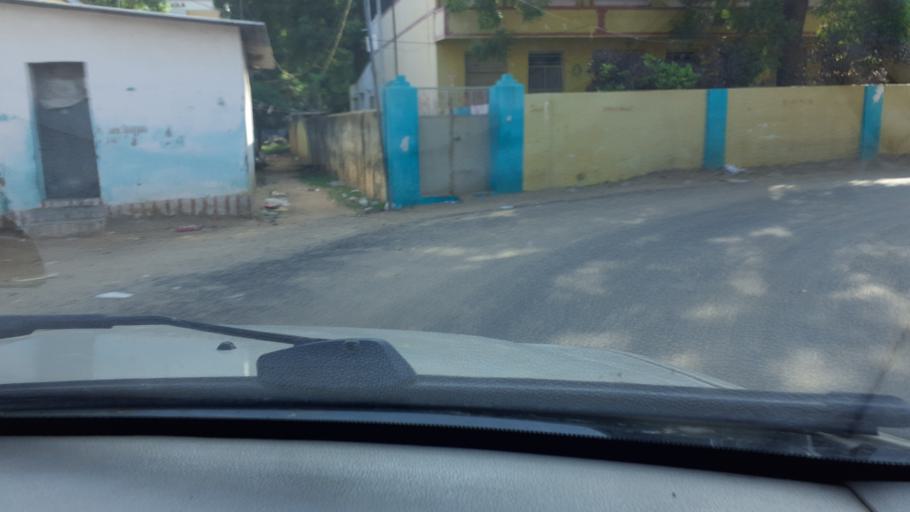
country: IN
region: Tamil Nadu
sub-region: Thoothukkudi
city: Eral
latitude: 8.5781
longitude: 78.0325
